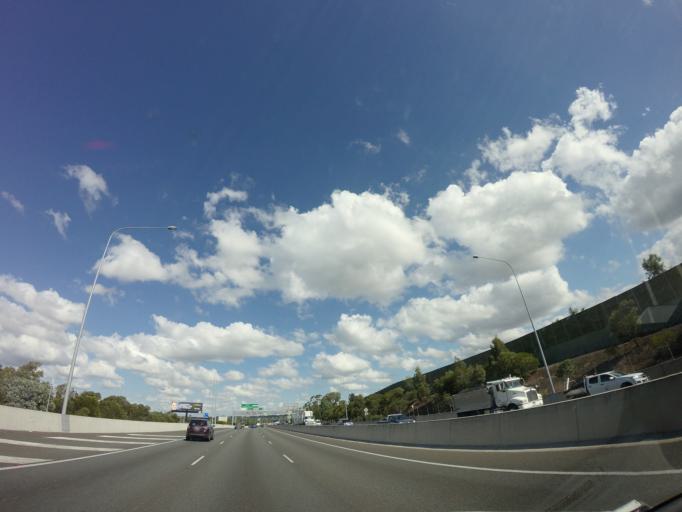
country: AU
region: Queensland
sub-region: Ipswich
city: Redbank
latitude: -27.6021
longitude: 152.8868
